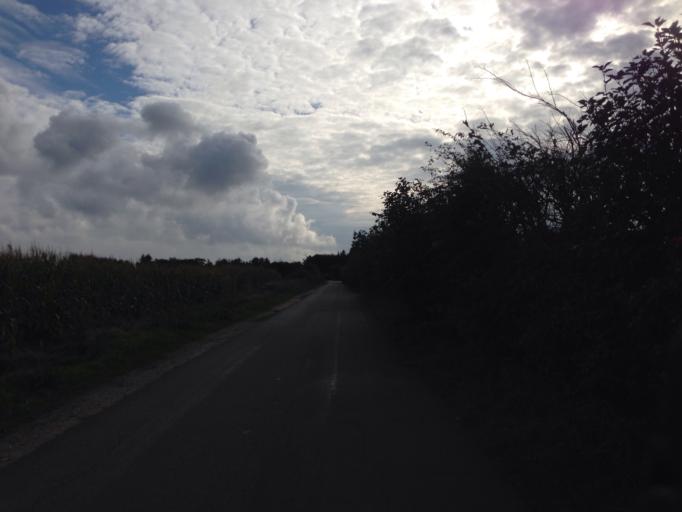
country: DE
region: Schleswig-Holstein
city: Utersum
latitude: 54.7148
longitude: 8.3997
